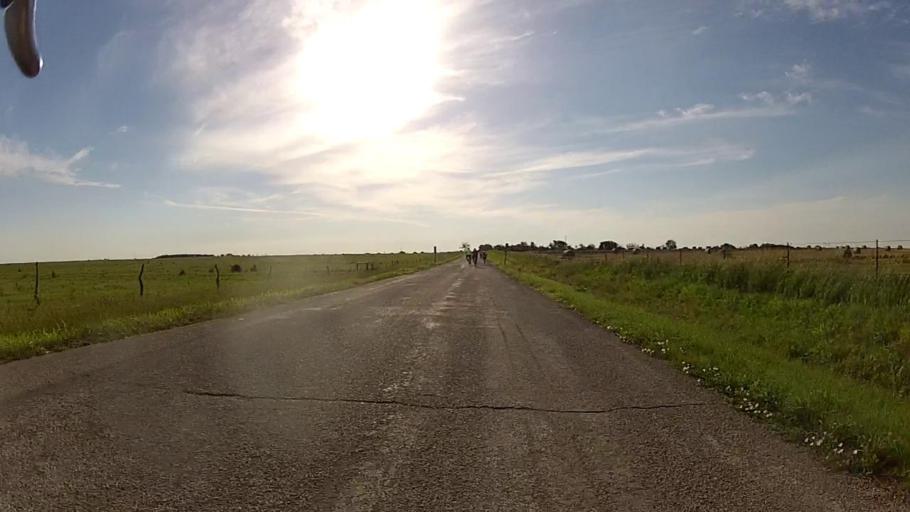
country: US
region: Kansas
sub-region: Cowley County
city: Arkansas City
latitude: 37.0557
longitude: -96.8184
